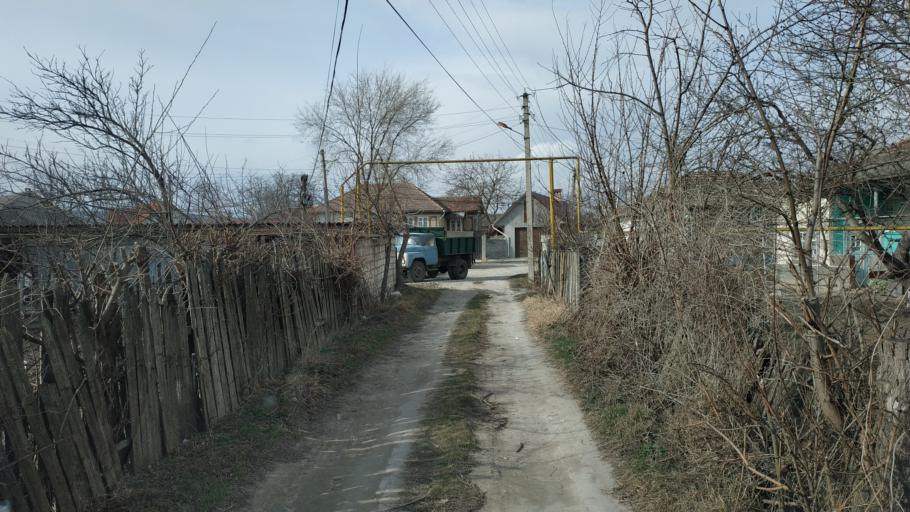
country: MD
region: Laloveni
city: Ialoveni
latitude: 46.8647
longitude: 28.7788
